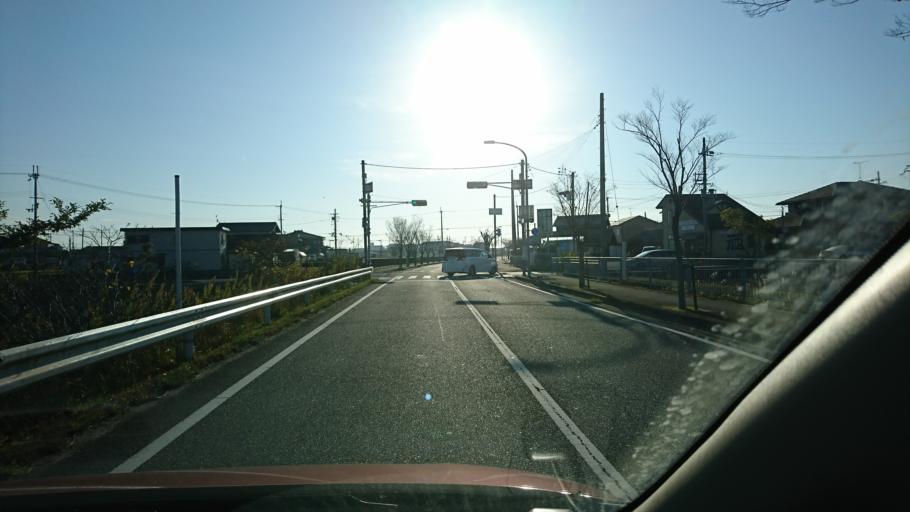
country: JP
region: Hyogo
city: Miki
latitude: 34.7715
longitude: 134.9092
